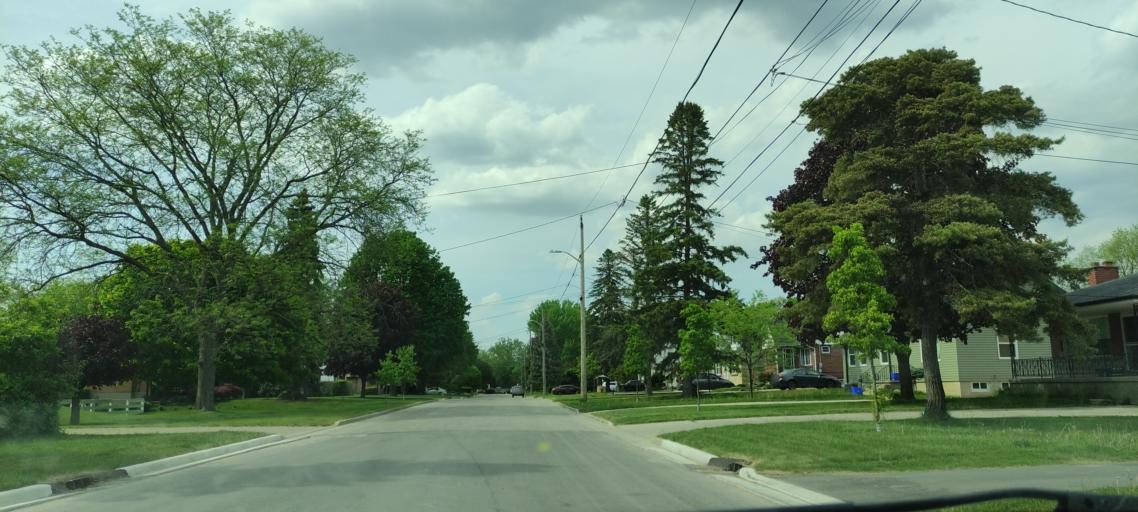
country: CA
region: Ontario
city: London
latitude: 43.0181
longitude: -81.2392
